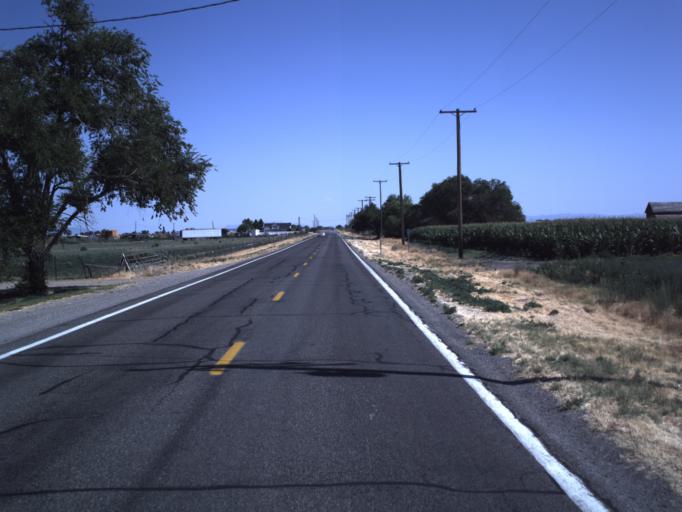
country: US
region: Utah
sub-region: Millard County
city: Delta
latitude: 39.2975
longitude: -112.6526
